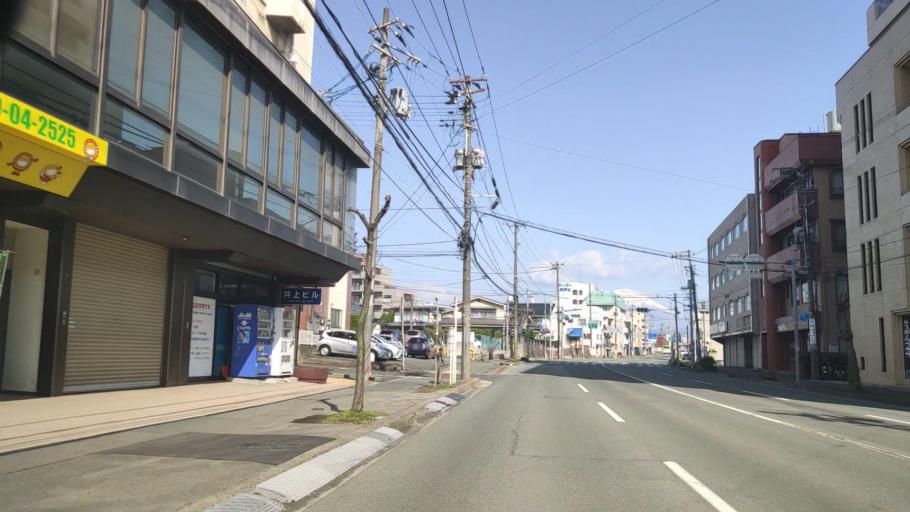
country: JP
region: Iwate
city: Morioka-shi
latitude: 39.7055
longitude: 141.1362
